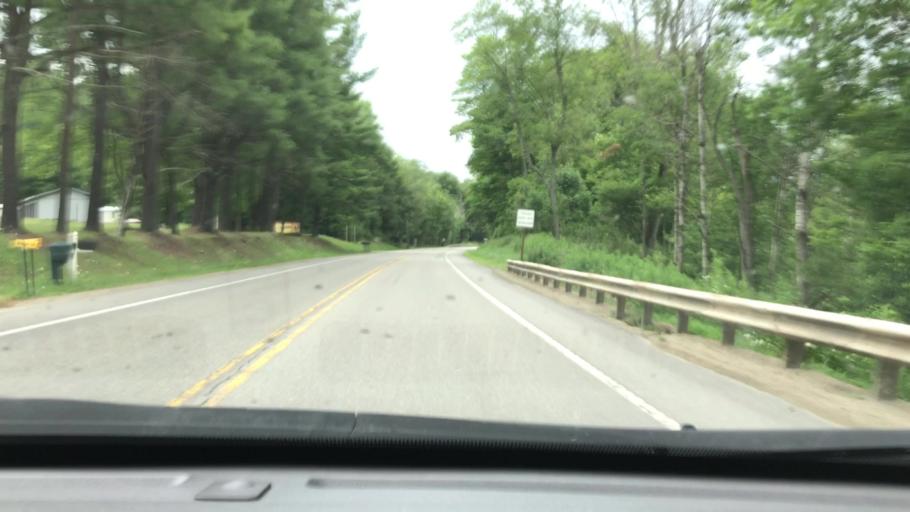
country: US
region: Pennsylvania
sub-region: McKean County
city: Bradford
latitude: 41.8597
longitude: -78.6726
